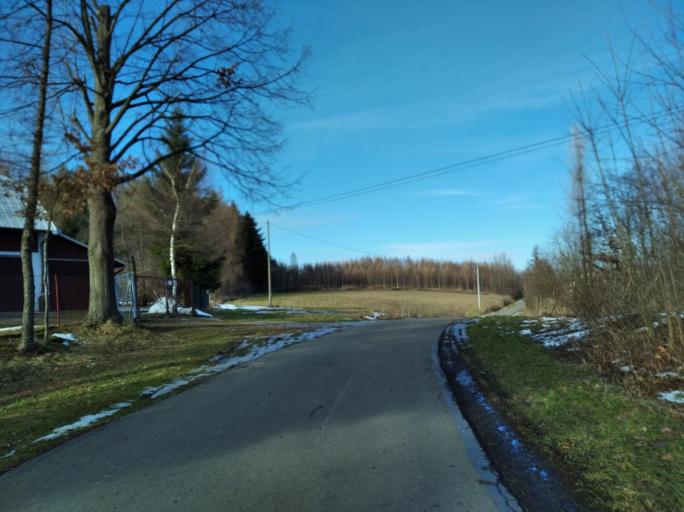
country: PL
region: Subcarpathian Voivodeship
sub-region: Powiat strzyzowski
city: Gwoznica Gorna
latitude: 49.8167
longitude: 21.9900
